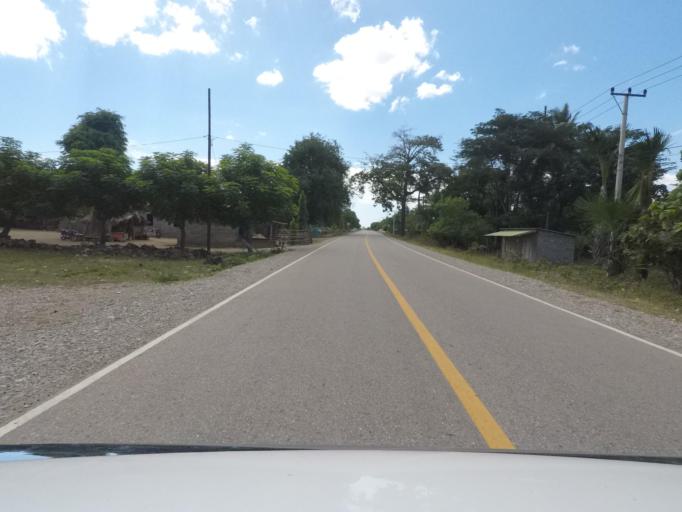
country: TL
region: Lautem
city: Lospalos
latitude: -8.4003
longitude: 126.8320
